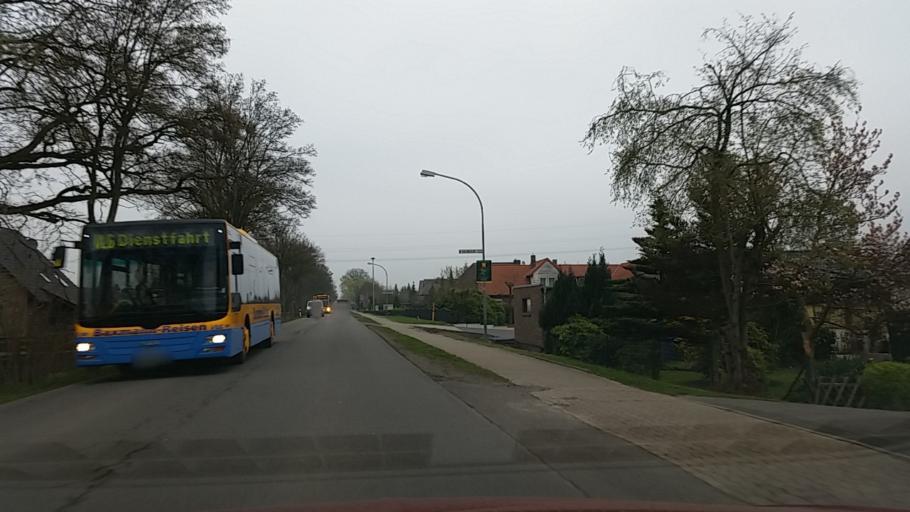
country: DE
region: Lower Saxony
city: Sassenburg
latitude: 52.5152
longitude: 10.5849
